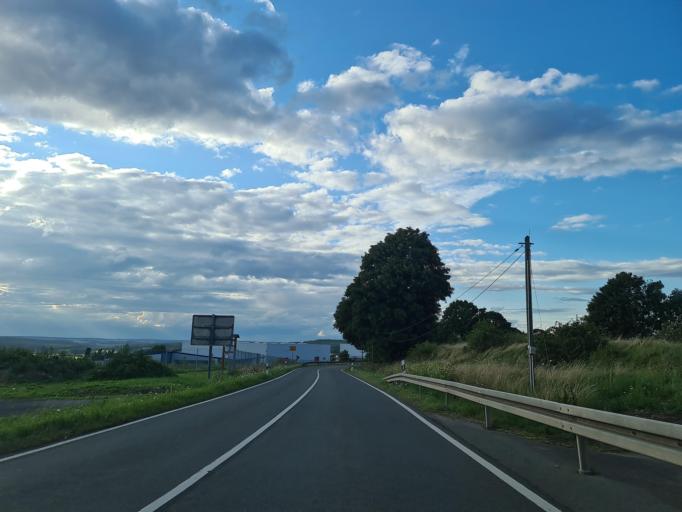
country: DE
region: Saxony
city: Pausa
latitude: 50.5885
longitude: 11.9986
